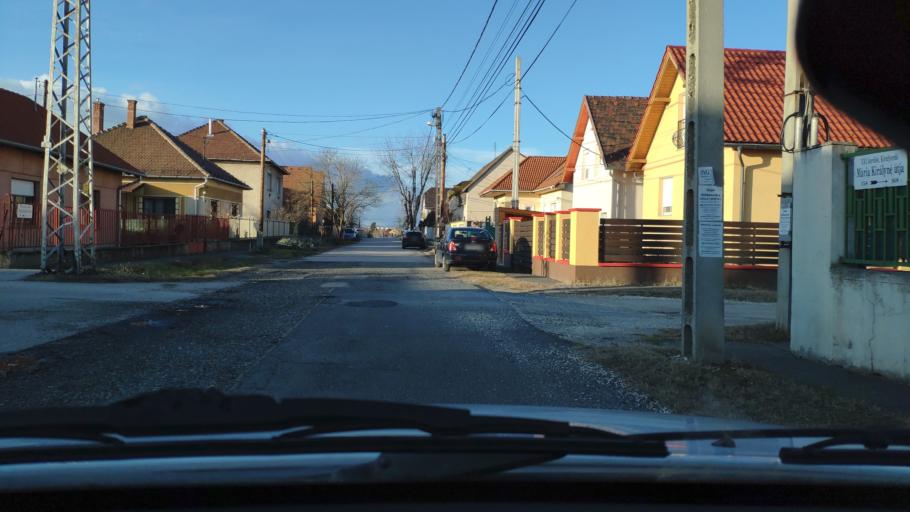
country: HU
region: Budapest
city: Budapest XXIII. keruelet
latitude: 47.3966
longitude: 19.0951
